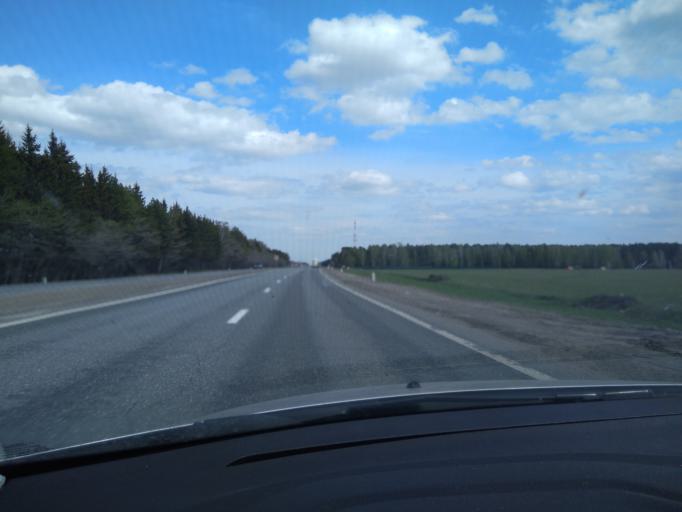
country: RU
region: Tjumen
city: Moskovskiy
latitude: 57.0958
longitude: 65.2172
